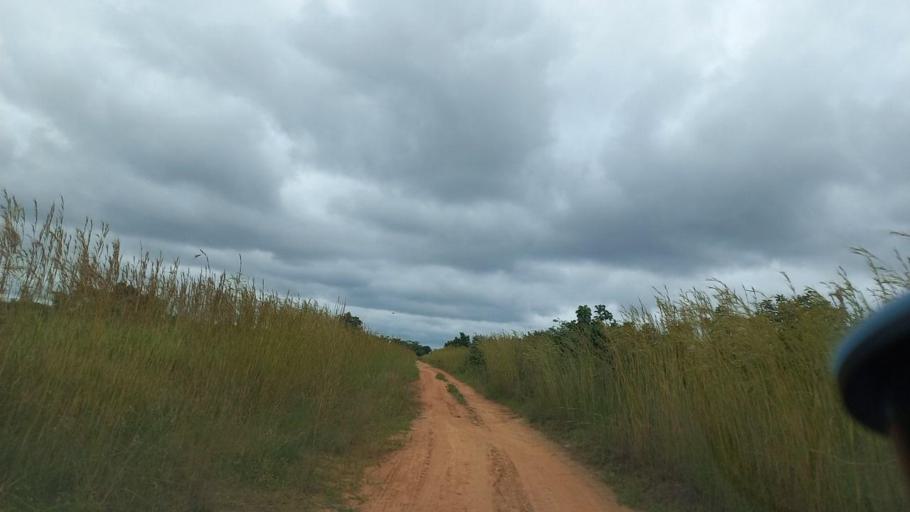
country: ZM
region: Lusaka
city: Lusaka
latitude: -15.1274
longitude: 28.3703
